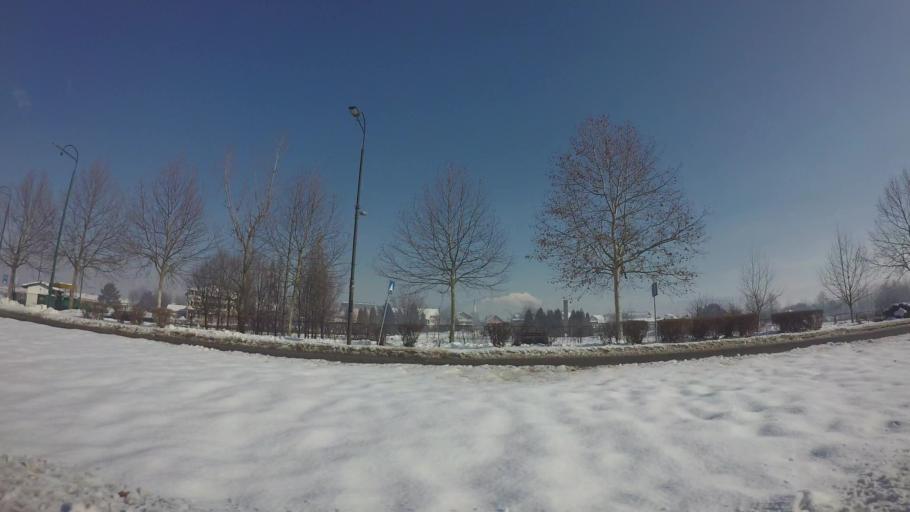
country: BA
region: Federation of Bosnia and Herzegovina
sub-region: Kanton Sarajevo
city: Sarajevo
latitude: 43.8102
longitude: 18.3101
